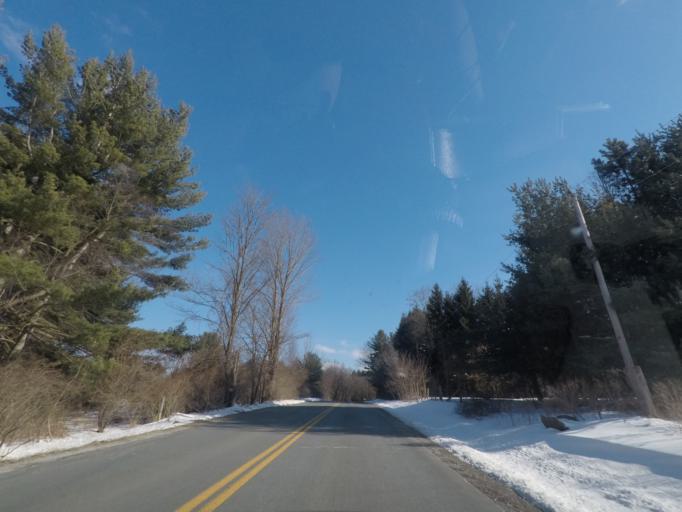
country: US
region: New York
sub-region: Rensselaer County
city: Hoosick Falls
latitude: 42.8955
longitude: -73.4993
